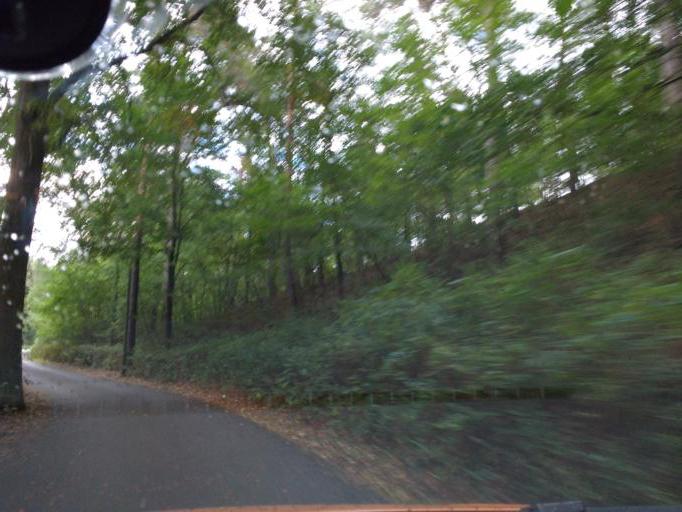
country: DE
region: Brandenburg
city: Storkow
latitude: 52.2670
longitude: 13.9599
